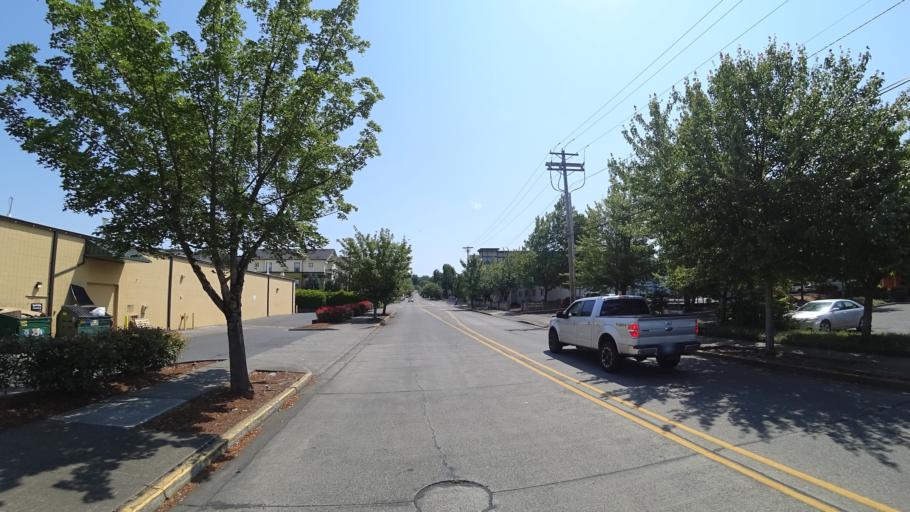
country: US
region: Oregon
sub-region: Clackamas County
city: Clackamas
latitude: 45.4413
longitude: -122.5775
